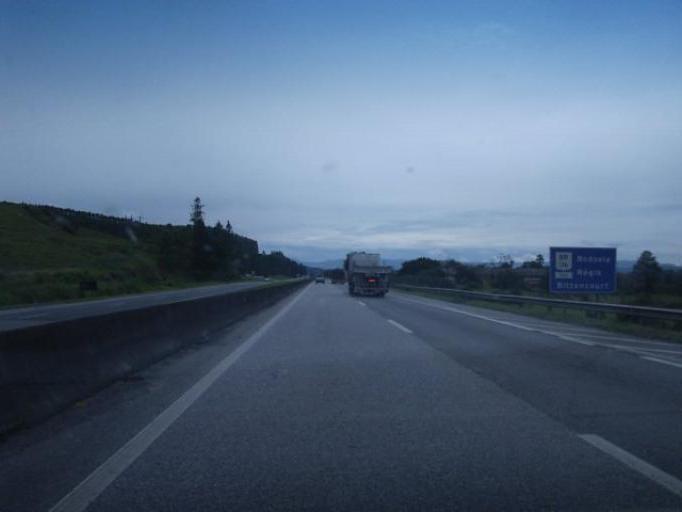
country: BR
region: Sao Paulo
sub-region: Jacupiranga
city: Jacupiranga
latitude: -24.7110
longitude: -48.0224
